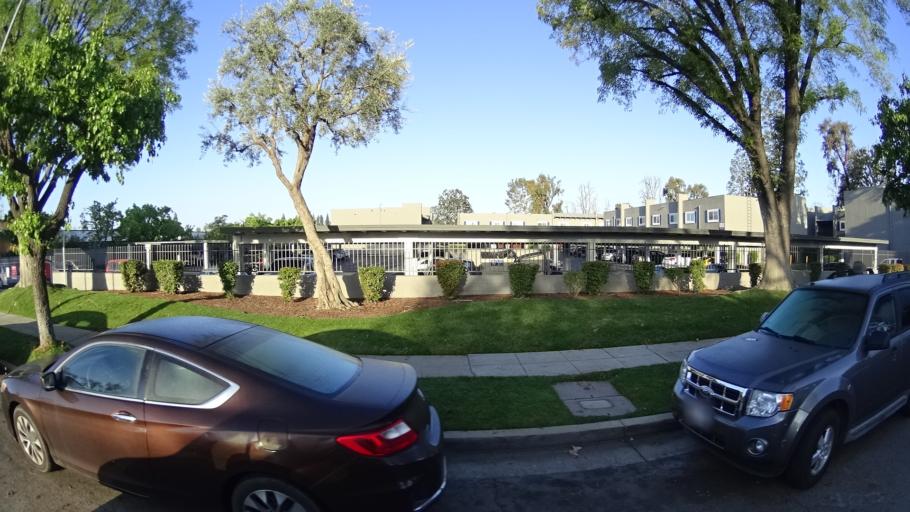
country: US
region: California
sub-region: Fresno County
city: Clovis
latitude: 36.8108
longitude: -119.7588
